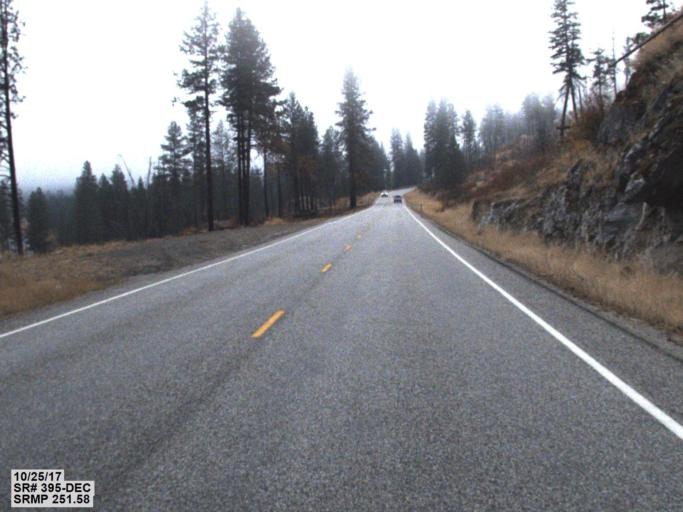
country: US
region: Washington
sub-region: Stevens County
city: Kettle Falls
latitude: 48.7590
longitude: -118.1374
